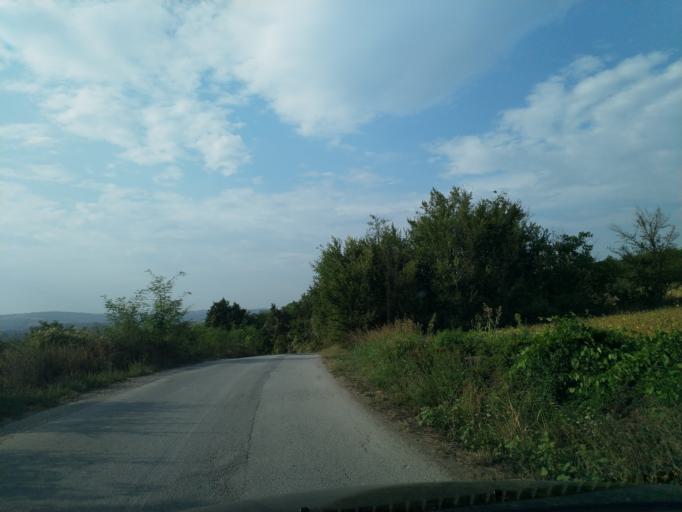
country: RS
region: Central Serbia
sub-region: Pomoravski Okrug
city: Paracin
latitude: 43.8431
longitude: 21.5295
